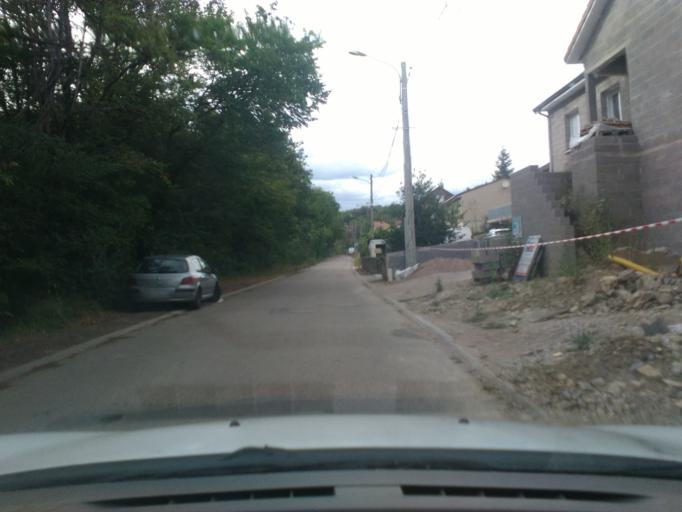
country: FR
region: Lorraine
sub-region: Departement des Vosges
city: Chatel-sur-Moselle
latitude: 48.3198
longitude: 6.3835
